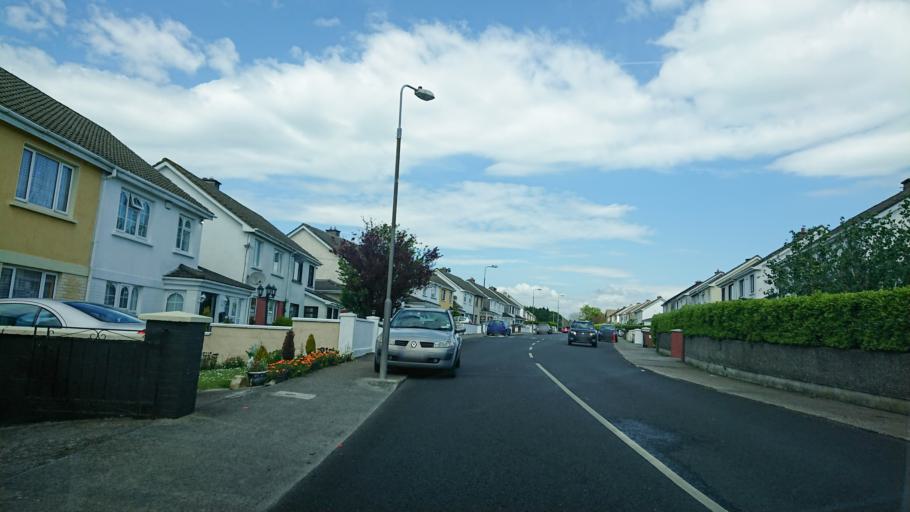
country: IE
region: Munster
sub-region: Waterford
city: Waterford
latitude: 52.2512
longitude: -7.1450
